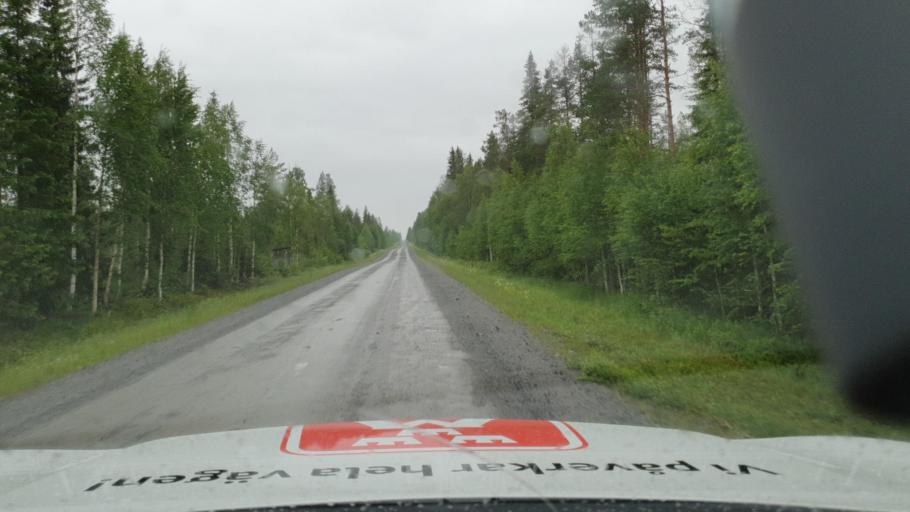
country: SE
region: Vaesterbotten
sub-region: Bjurholms Kommun
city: Bjurholm
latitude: 63.8459
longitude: 19.4786
